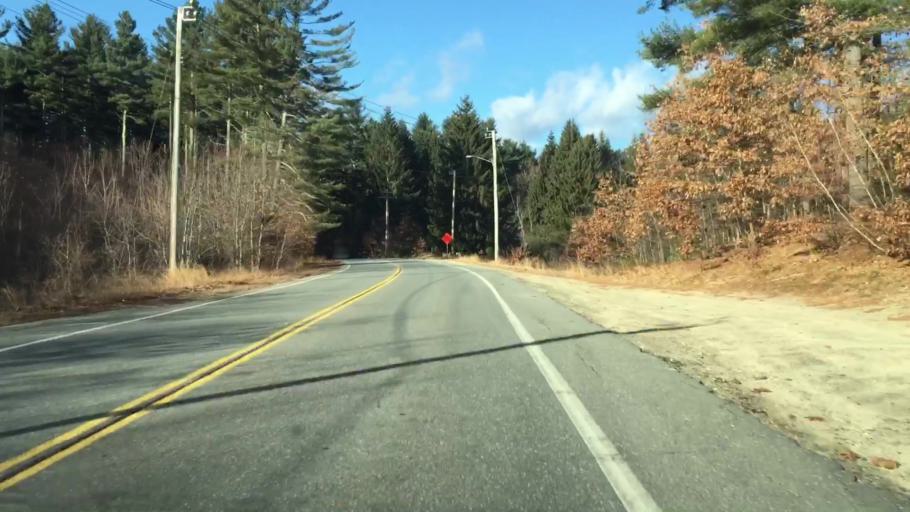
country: US
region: Massachusetts
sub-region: Worcester County
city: West Boylston
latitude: 42.3790
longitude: -71.7836
